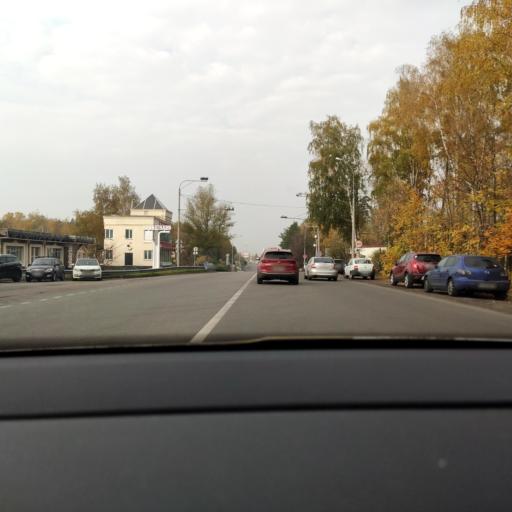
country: RU
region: Moskovskaya
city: Lesnyye Polyany
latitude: 55.9834
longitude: 37.8850
